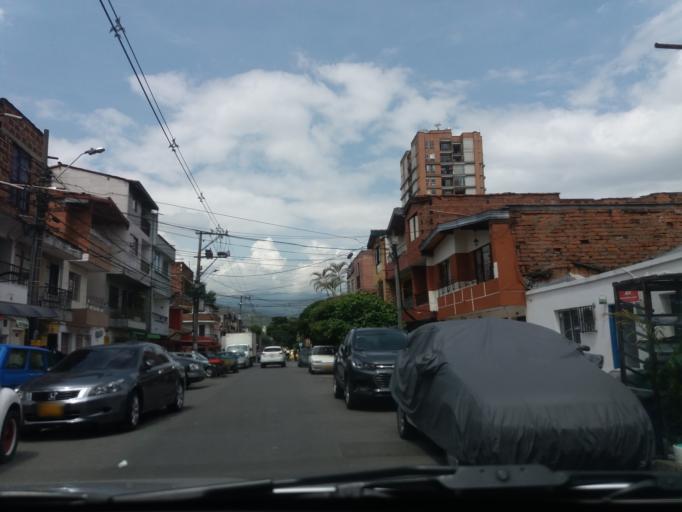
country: CO
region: Antioquia
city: Itagui
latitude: 6.2045
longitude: -75.5826
